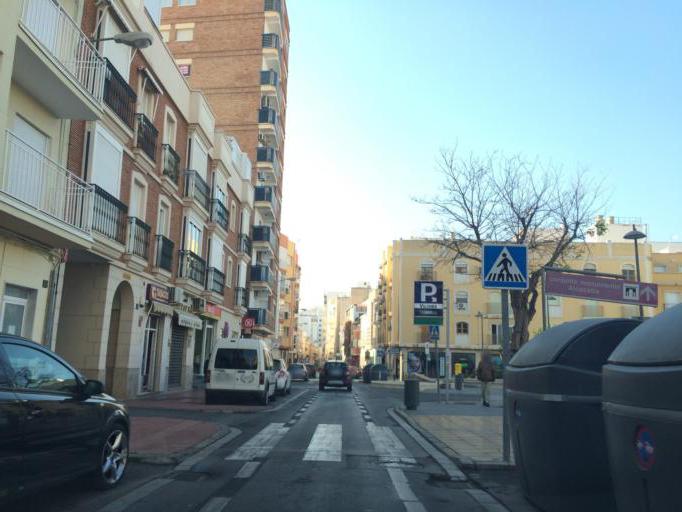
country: ES
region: Andalusia
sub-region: Provincia de Almeria
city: Almeria
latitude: 36.8449
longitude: -2.4604
